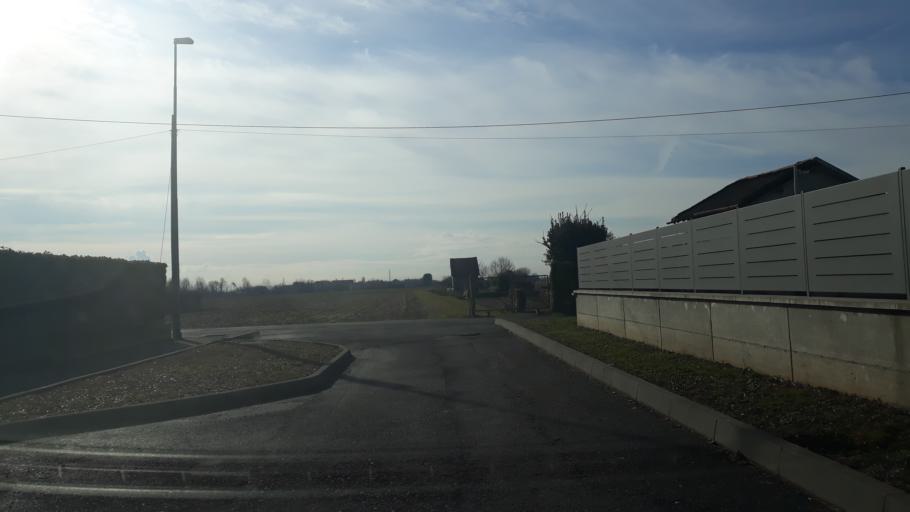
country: IT
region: Lombardy
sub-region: Provincia di Monza e Brianza
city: Aicurzio
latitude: 45.6333
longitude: 9.4079
